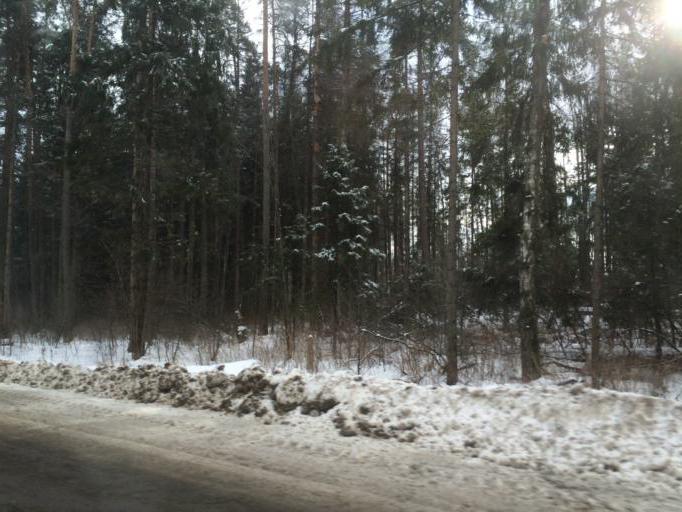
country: RU
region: Moskovskaya
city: Pavlovskaya Sloboda
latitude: 55.7976
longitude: 37.1372
